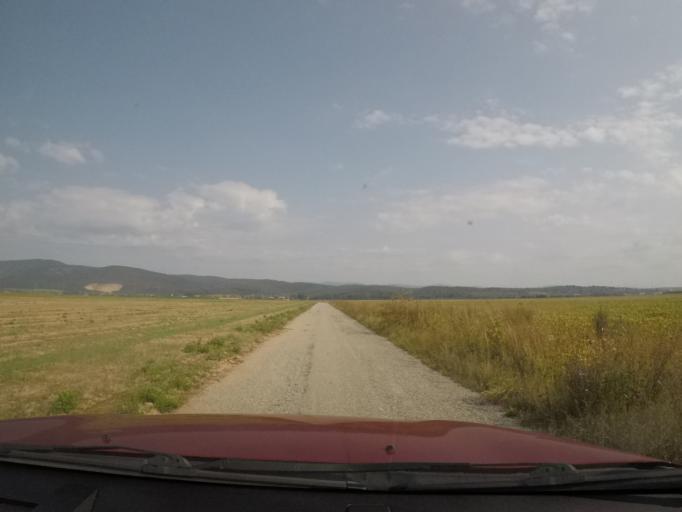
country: SK
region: Kosicky
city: Moldava nad Bodvou
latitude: 48.5901
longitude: 20.9569
